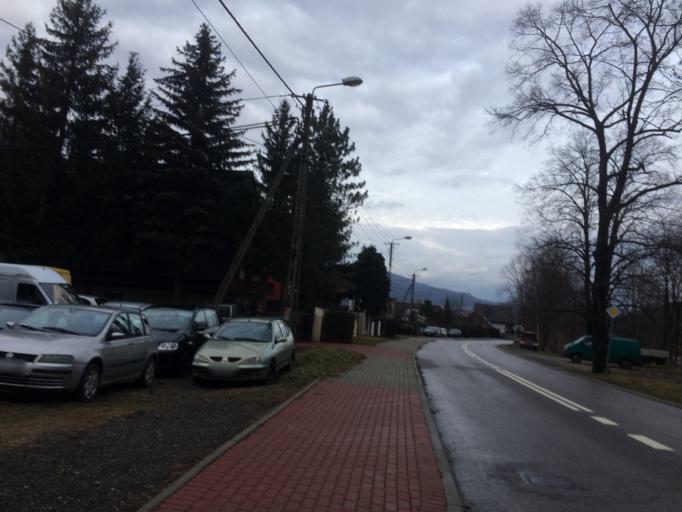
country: PL
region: Silesian Voivodeship
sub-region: Powiat bielski
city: Bystra
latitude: 49.7603
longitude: 19.0396
